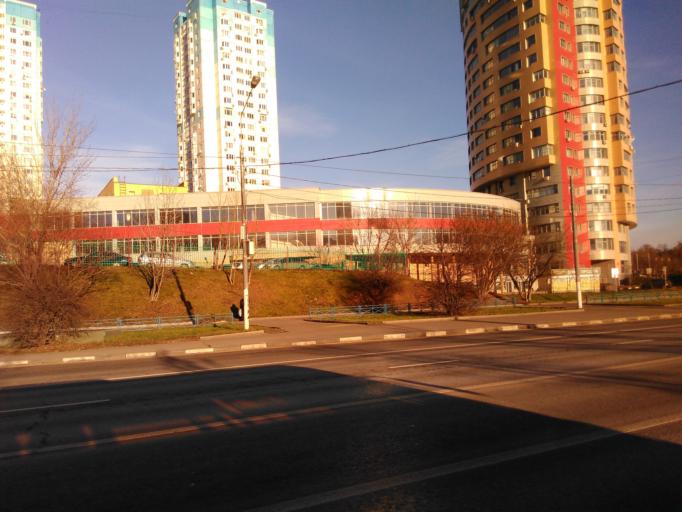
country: RU
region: Moscow
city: Nagornyy
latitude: 55.6416
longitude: 37.6026
